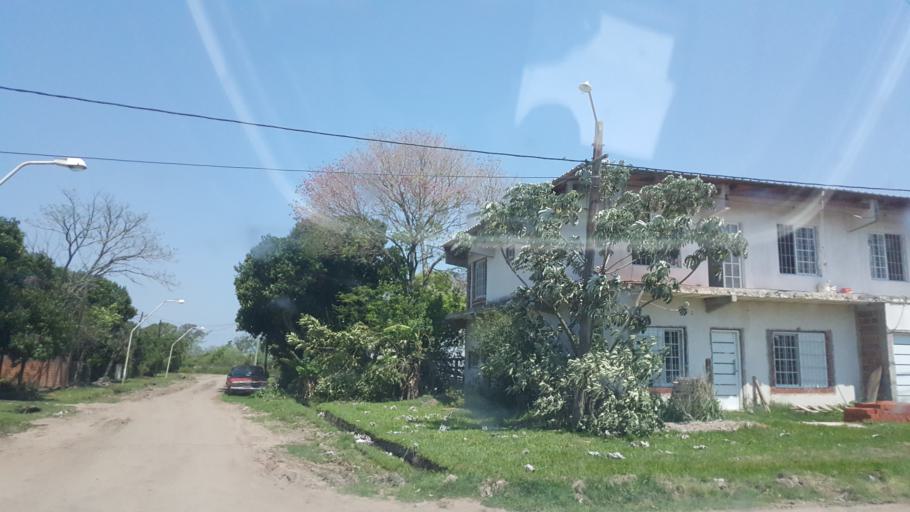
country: AR
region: Corrientes
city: Ita Ibate
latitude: -27.4265
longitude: -57.3293
